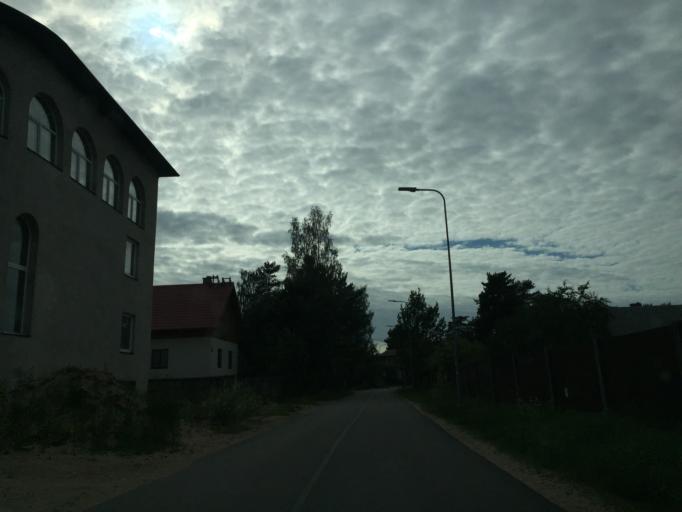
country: LV
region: Carnikava
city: Carnikava
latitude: 57.1320
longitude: 24.2547
